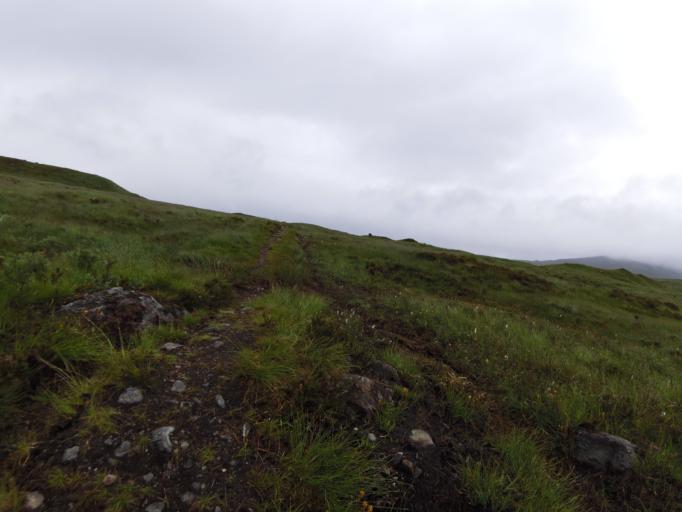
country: GB
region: Scotland
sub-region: Highland
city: Spean Bridge
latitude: 56.7687
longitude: -4.7049
